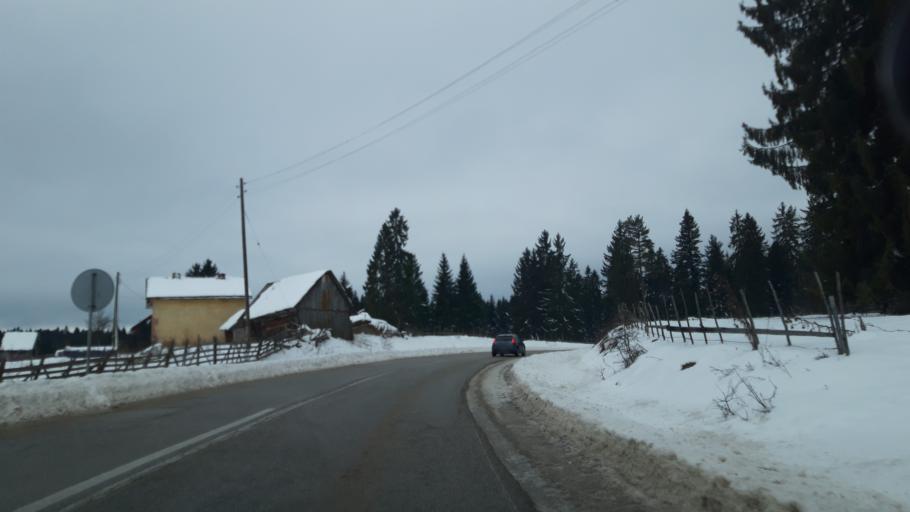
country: BA
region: Republika Srpska
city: Han Pijesak
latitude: 44.0250
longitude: 18.8979
